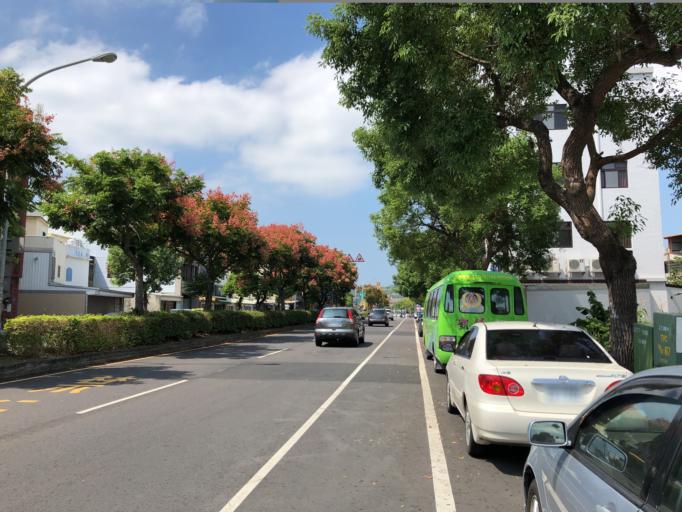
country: TW
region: Taiwan
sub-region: Miaoli
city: Miaoli
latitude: 24.5741
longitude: 120.8300
